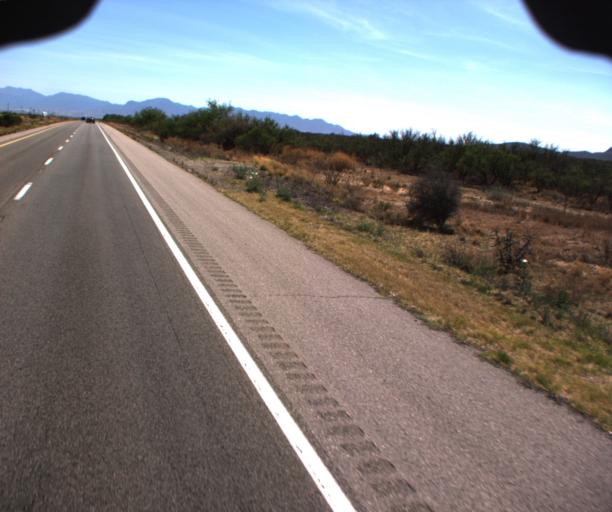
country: US
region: Arizona
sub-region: Cochise County
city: Huachuca City
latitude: 31.7408
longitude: -110.3503
